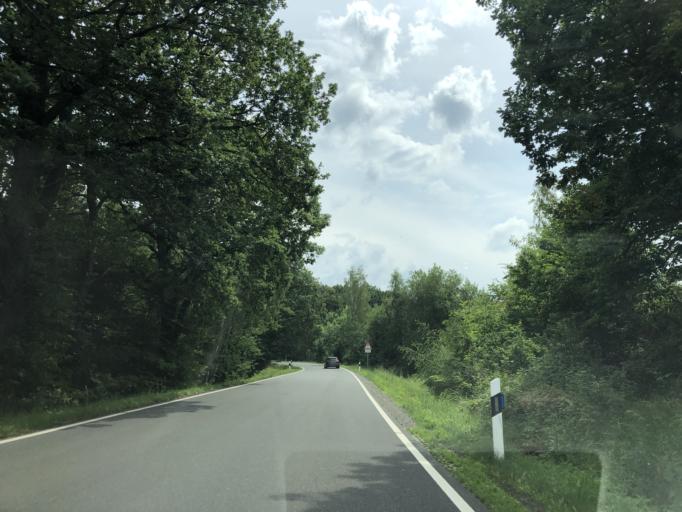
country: DE
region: Hesse
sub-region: Regierungsbezirk Darmstadt
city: Brensbach
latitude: 49.7535
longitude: 8.9101
